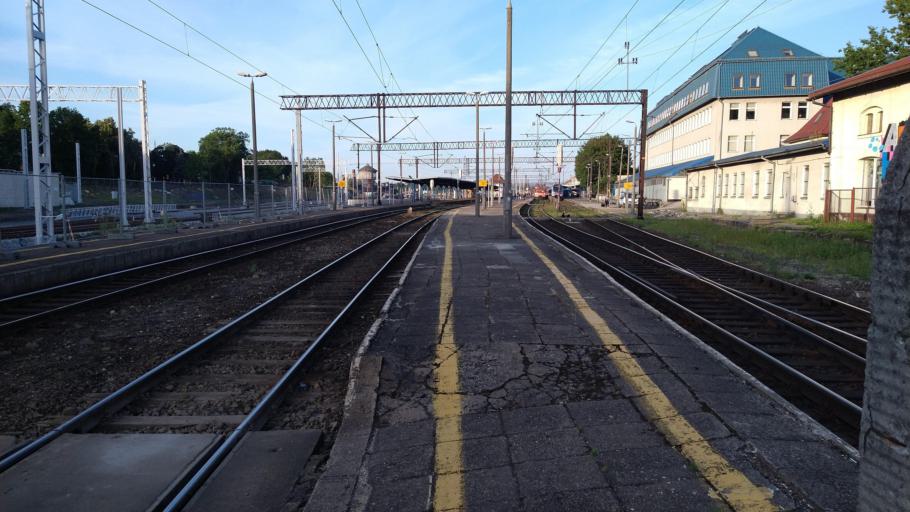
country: PL
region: Warmian-Masurian Voivodeship
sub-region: Powiat olsztynski
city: Olsztyn
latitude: 53.7849
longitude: 20.4940
